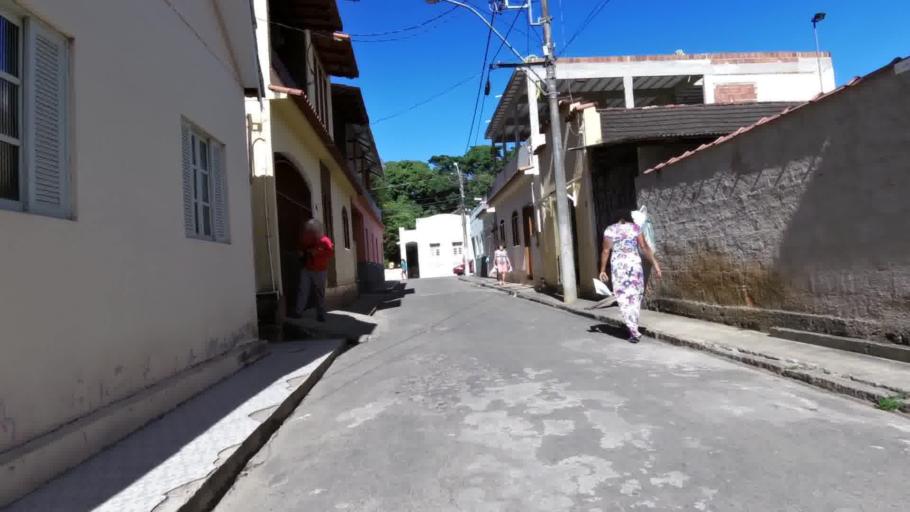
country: BR
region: Espirito Santo
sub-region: Rio Novo Do Sul
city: Rio Novo do Sul
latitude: -20.8633
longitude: -40.9343
